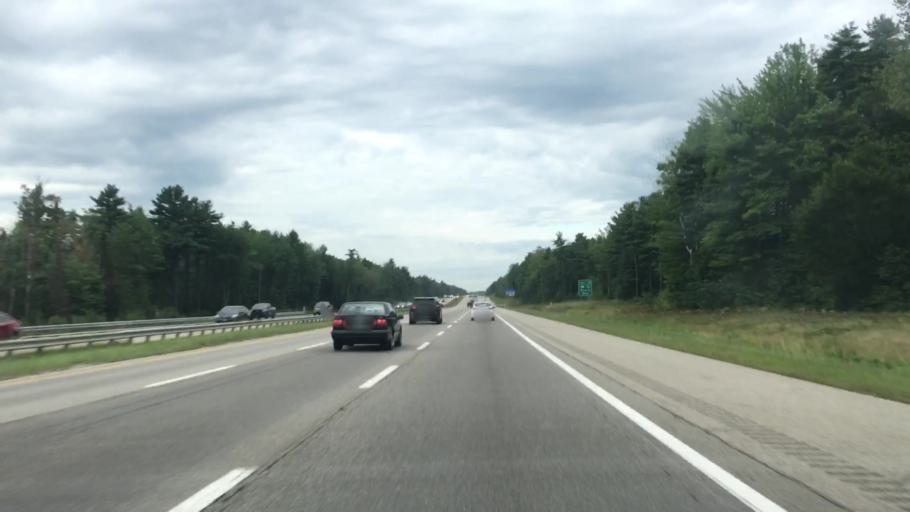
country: US
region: Maine
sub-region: Cumberland County
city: West Scarborough
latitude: 43.5508
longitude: -70.4287
